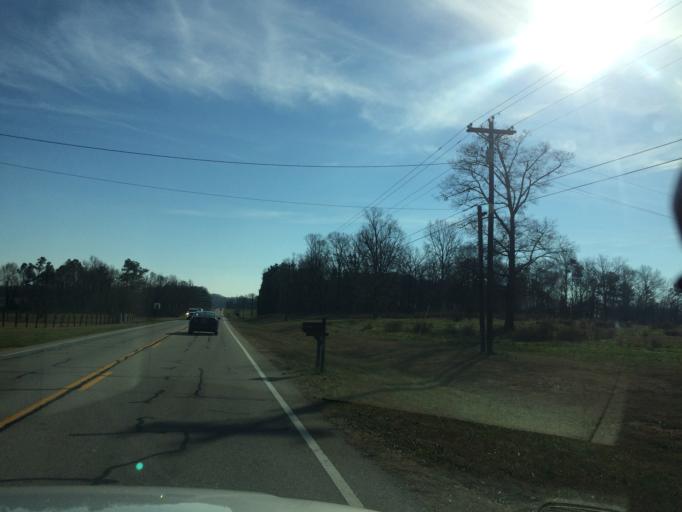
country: US
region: Georgia
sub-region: Franklin County
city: Lavonia
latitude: 34.4202
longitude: -83.0264
